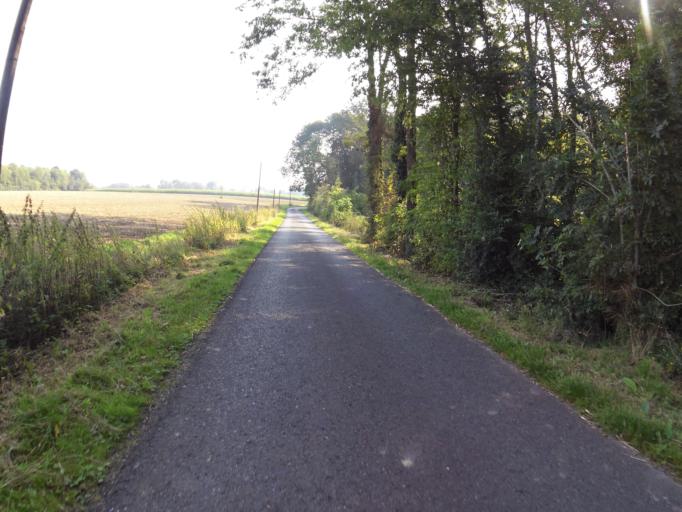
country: DE
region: North Rhine-Westphalia
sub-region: Regierungsbezirk Munster
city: Nottuln
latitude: 51.9825
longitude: 7.3488
